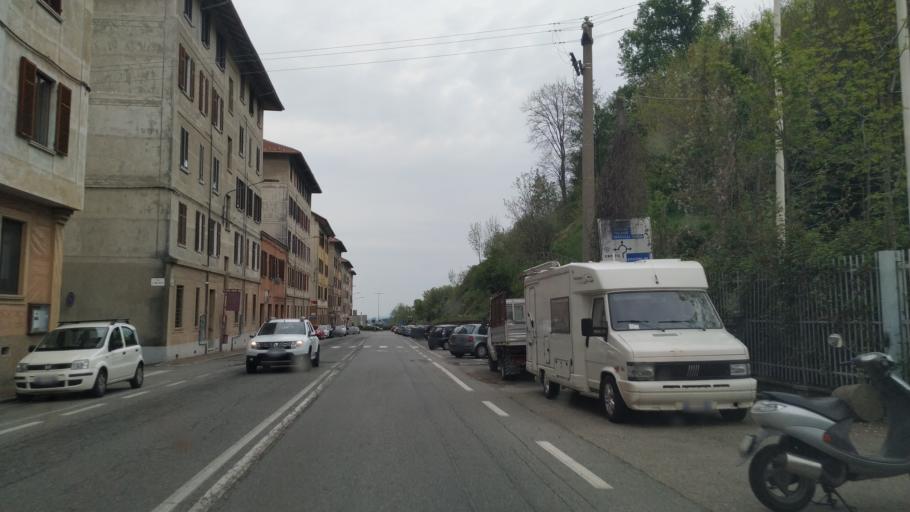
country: IT
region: Piedmont
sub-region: Provincia di Biella
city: Occhieppo Inferiore
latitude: 45.5579
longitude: 8.0272
